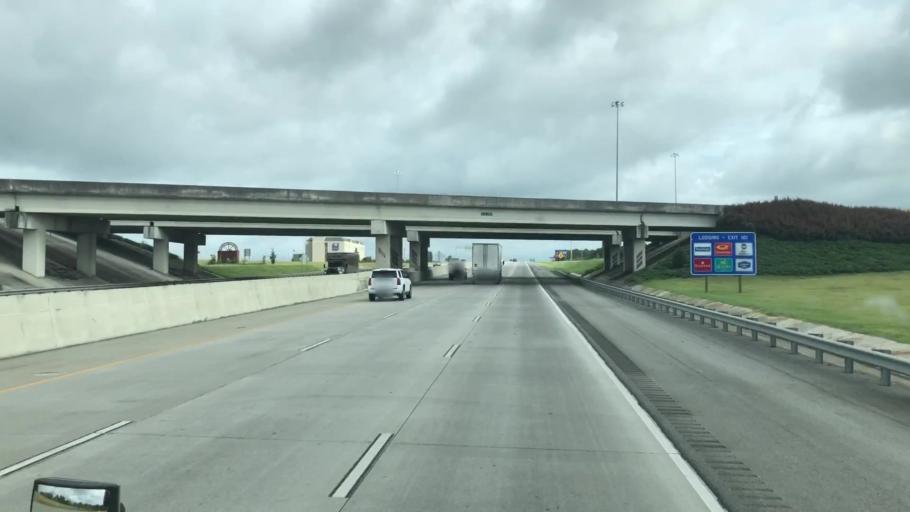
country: US
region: Georgia
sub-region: Crisp County
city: Cordele
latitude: 31.9338
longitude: -83.7472
